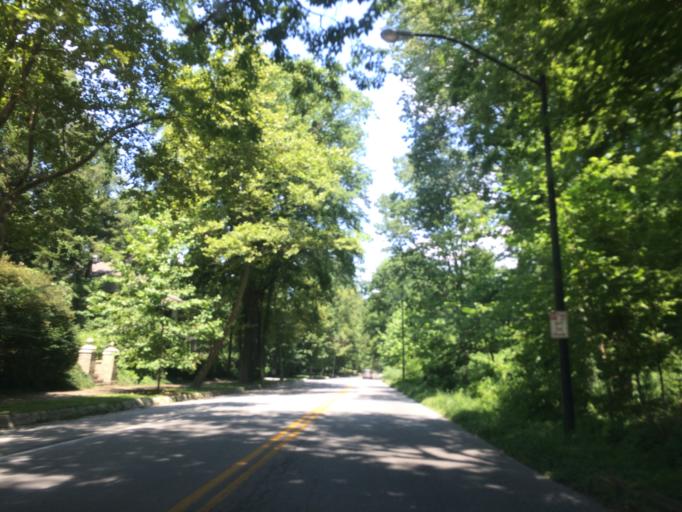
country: US
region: Kentucky
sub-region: Jefferson County
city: Audubon Park
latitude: 38.2394
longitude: -85.7067
